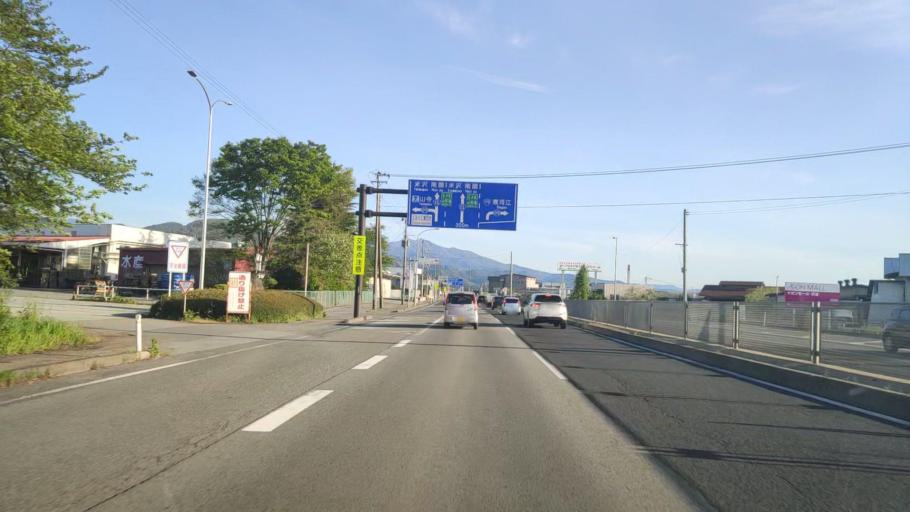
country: JP
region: Yamagata
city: Tendo
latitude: 38.3157
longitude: 140.3626
